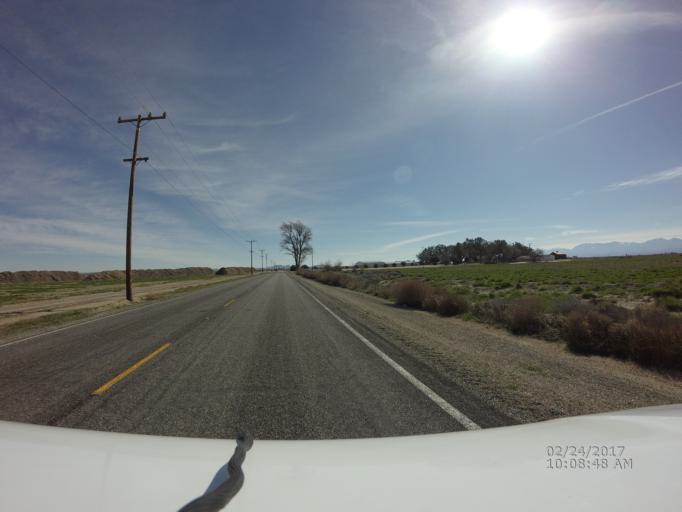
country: US
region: California
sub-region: Los Angeles County
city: Lancaster
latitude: 34.6753
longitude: -118.0129
